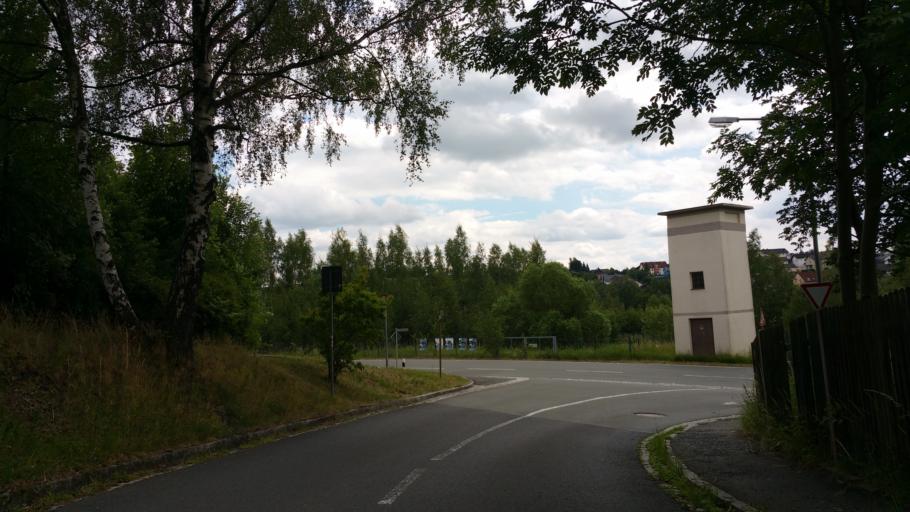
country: DE
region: Bavaria
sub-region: Upper Franconia
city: Oberkotzau
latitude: 50.2657
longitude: 11.9438
